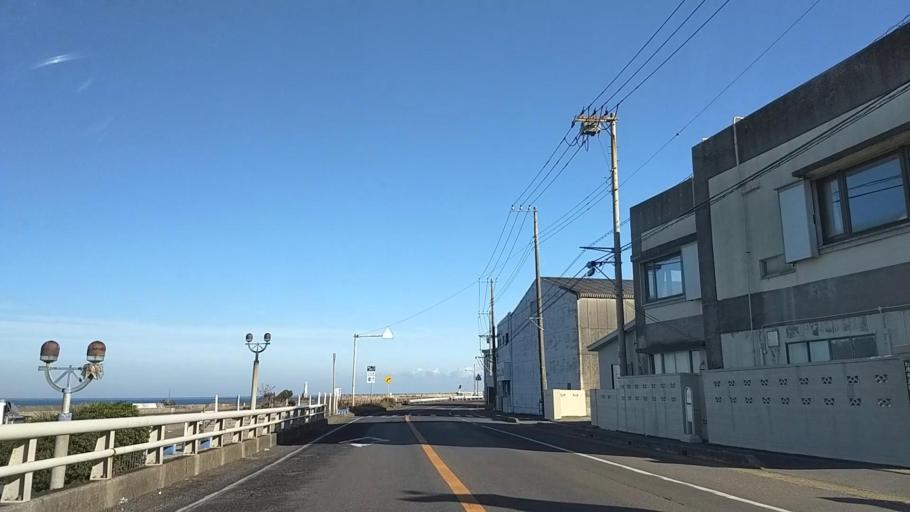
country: JP
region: Chiba
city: Hasaki
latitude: 35.7412
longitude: 140.8547
